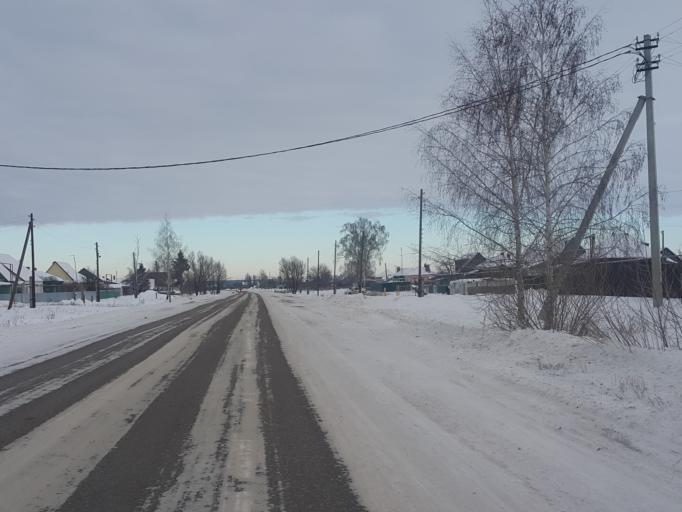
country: RU
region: Tambov
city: Platonovka
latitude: 52.8310
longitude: 41.8080
